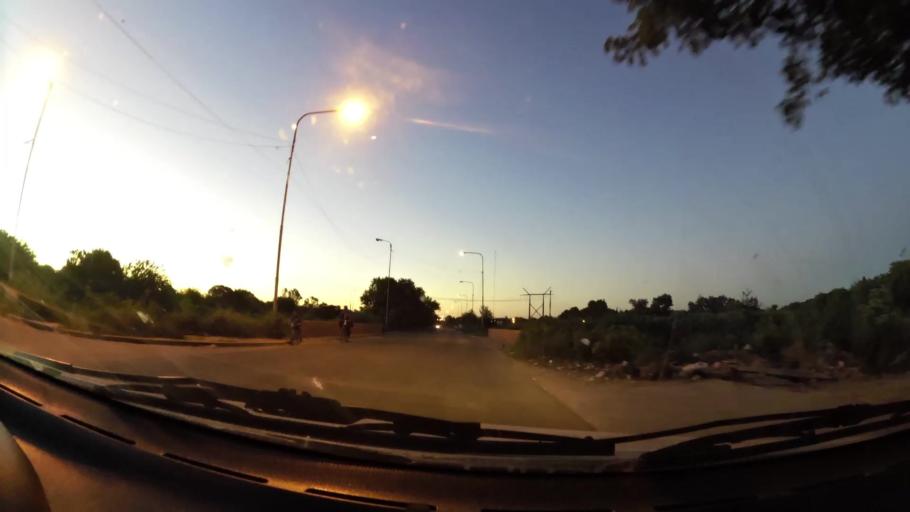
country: AR
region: Buenos Aires
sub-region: Partido de Quilmes
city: Quilmes
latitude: -34.7907
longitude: -58.1803
